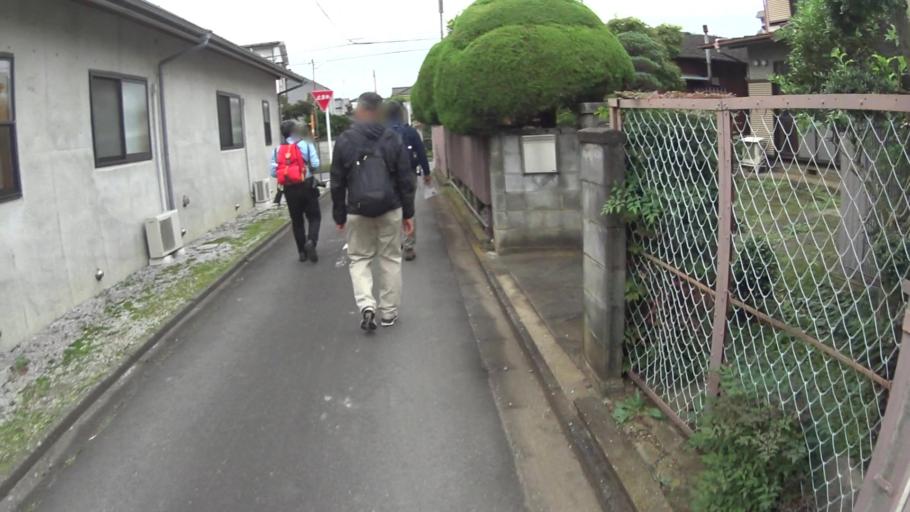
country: JP
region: Saitama
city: Hanno
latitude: 35.8551
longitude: 139.3243
